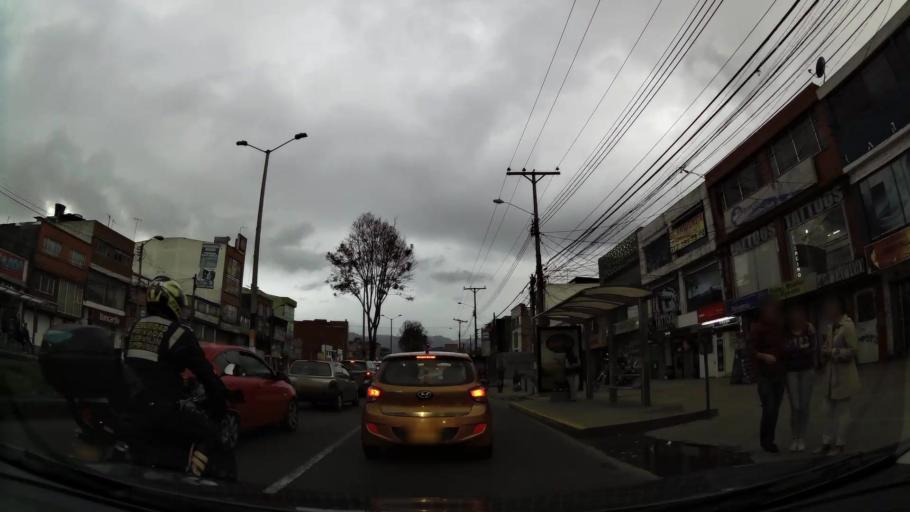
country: CO
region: Bogota D.C.
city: Barrio San Luis
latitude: 4.6916
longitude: -74.1005
